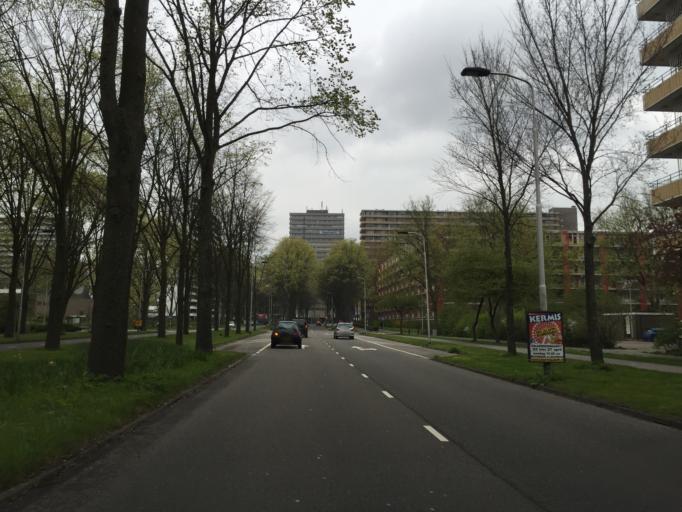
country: NL
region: South Holland
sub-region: Gemeente Delft
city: Delft
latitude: 51.9938
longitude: 4.3561
